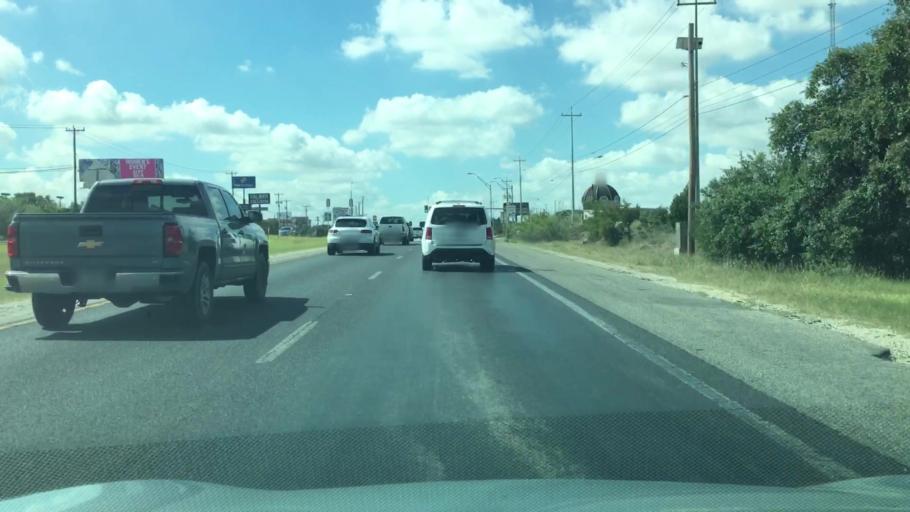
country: US
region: Texas
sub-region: Bexar County
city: Timberwood Park
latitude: 29.6648
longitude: -98.4503
